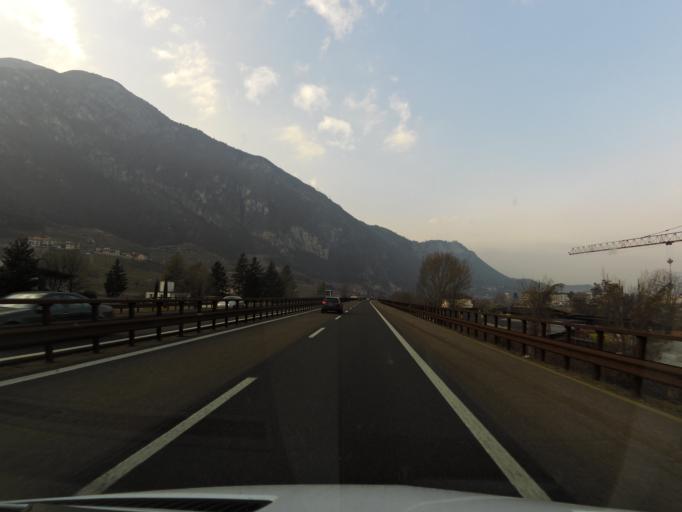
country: IT
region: Trentino-Alto Adige
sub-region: Provincia di Trento
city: Ravina
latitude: 46.0442
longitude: 11.1142
